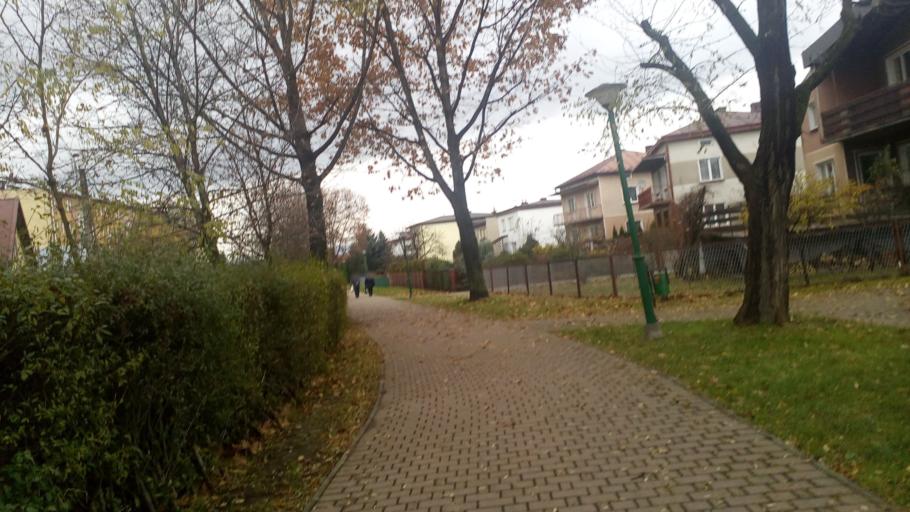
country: PL
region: Lesser Poland Voivodeship
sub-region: Powiat nowosadecki
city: Stary Sacz
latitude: 49.5673
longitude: 20.6295
